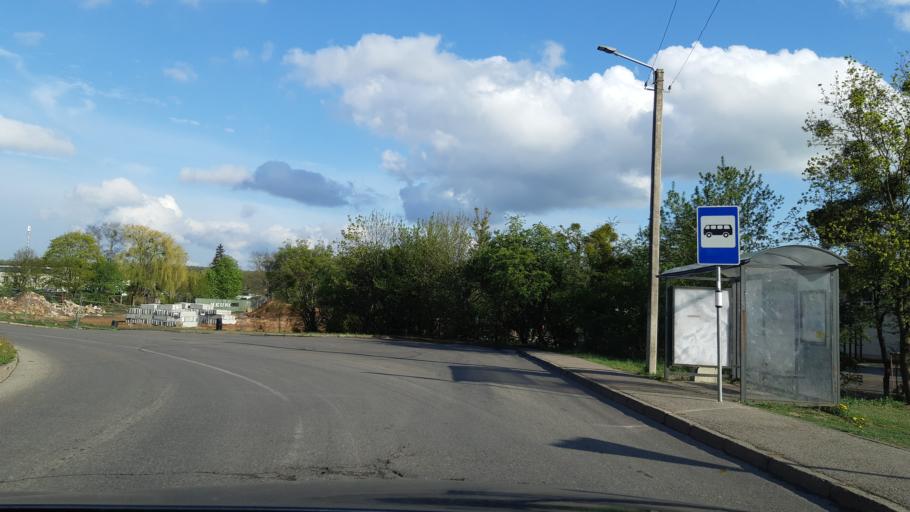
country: LT
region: Kauno apskritis
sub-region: Kaunas
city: Aleksotas
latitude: 54.8626
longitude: 23.9426
